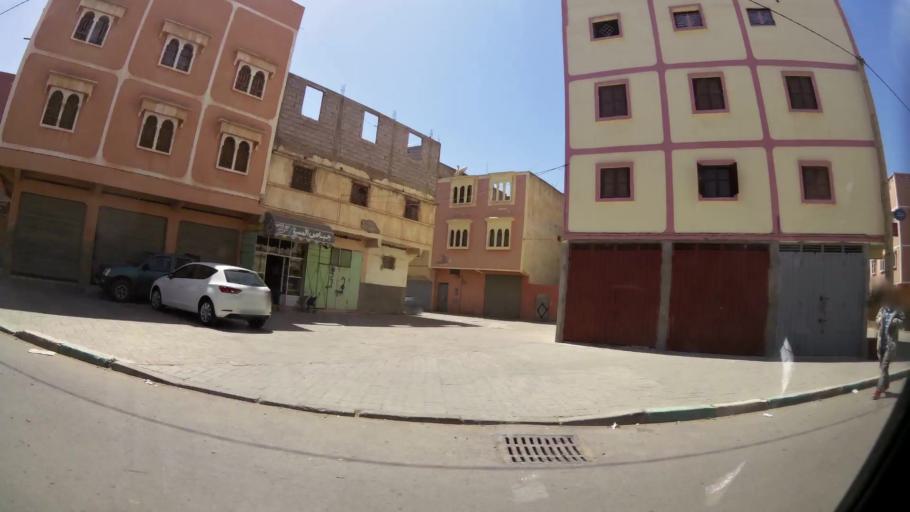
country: MA
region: Souss-Massa-Draa
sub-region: Inezgane-Ait Mellou
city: Inezgane
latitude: 30.3427
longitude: -9.4854
